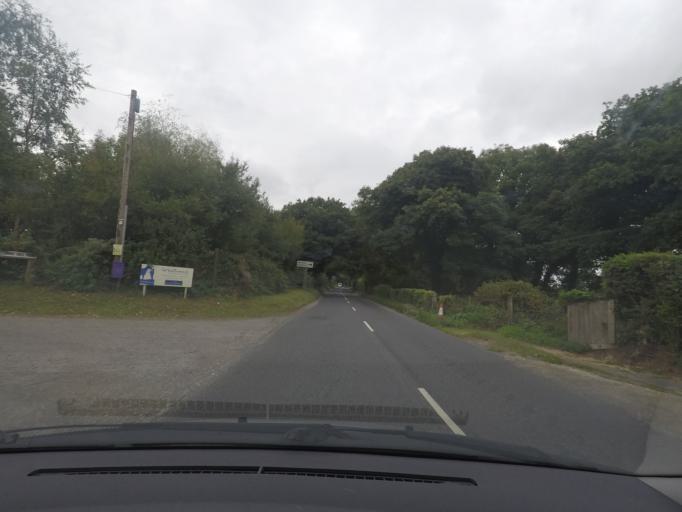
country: GB
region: England
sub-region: Wiltshire
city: Huish
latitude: 51.3851
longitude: -1.7577
